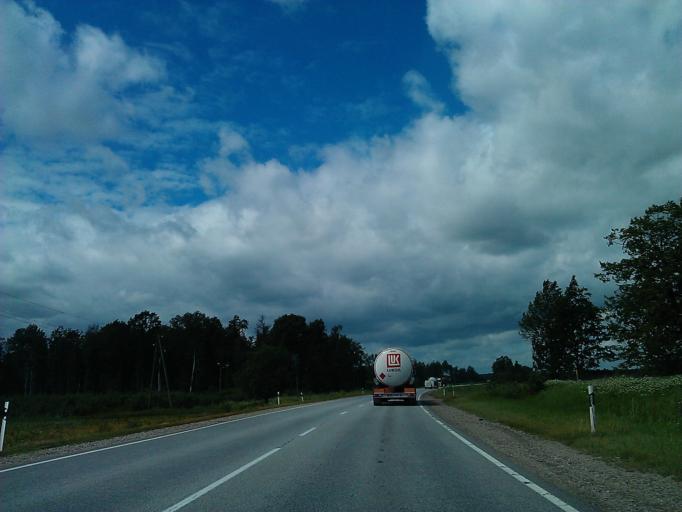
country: LV
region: Engure
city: Smarde
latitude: 56.9123
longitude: 23.3545
